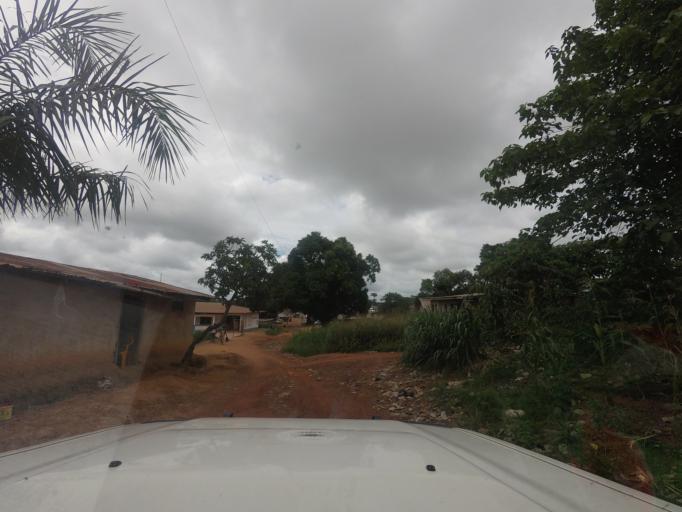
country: LR
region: Grand Gedeh
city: Zwedru
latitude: 6.0713
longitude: -8.1357
